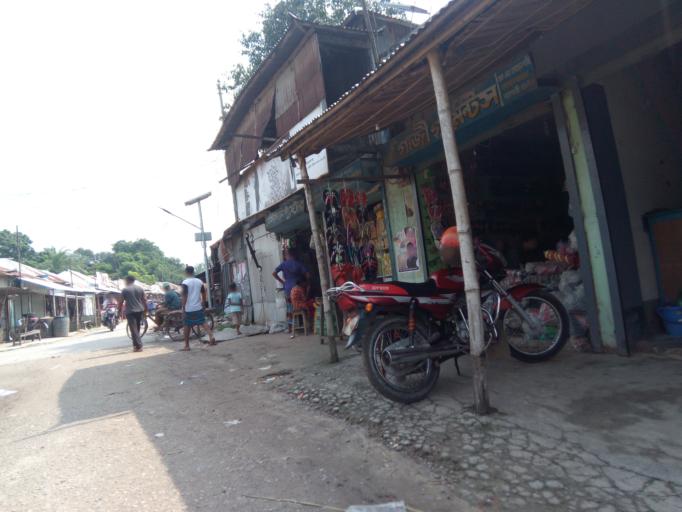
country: BD
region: Khulna
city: Kalia
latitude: 23.0839
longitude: 89.6697
